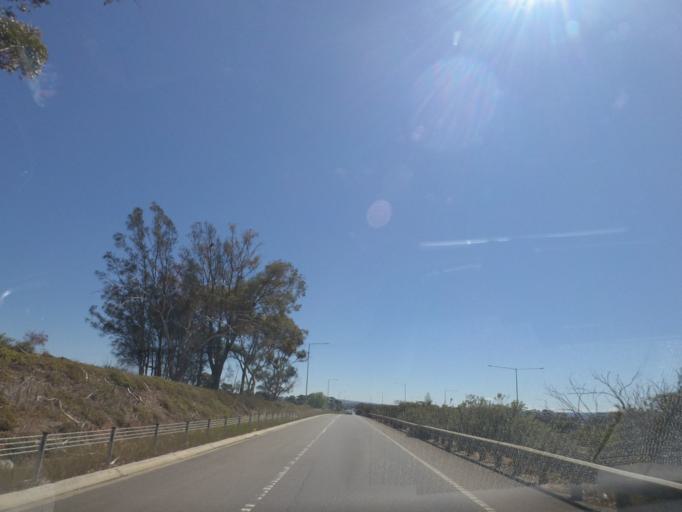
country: AU
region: Victoria
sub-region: Hume
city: Craigieburn
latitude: -37.5687
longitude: 144.9406
